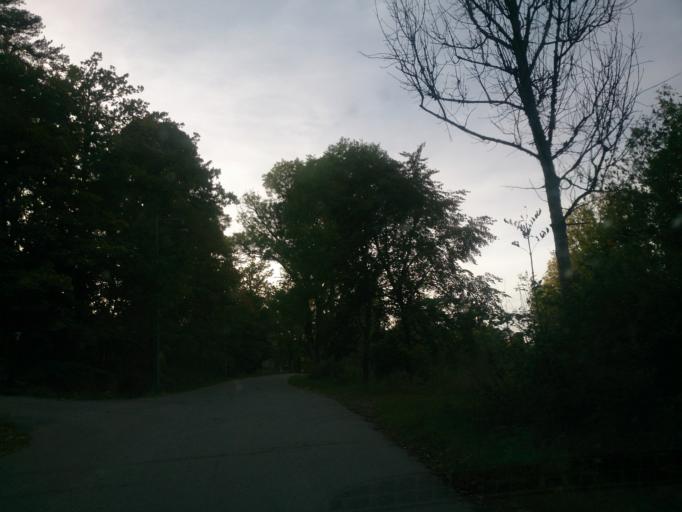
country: SE
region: Stockholm
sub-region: Nacka Kommun
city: Saltsjobaden
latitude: 59.2366
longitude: 18.2963
